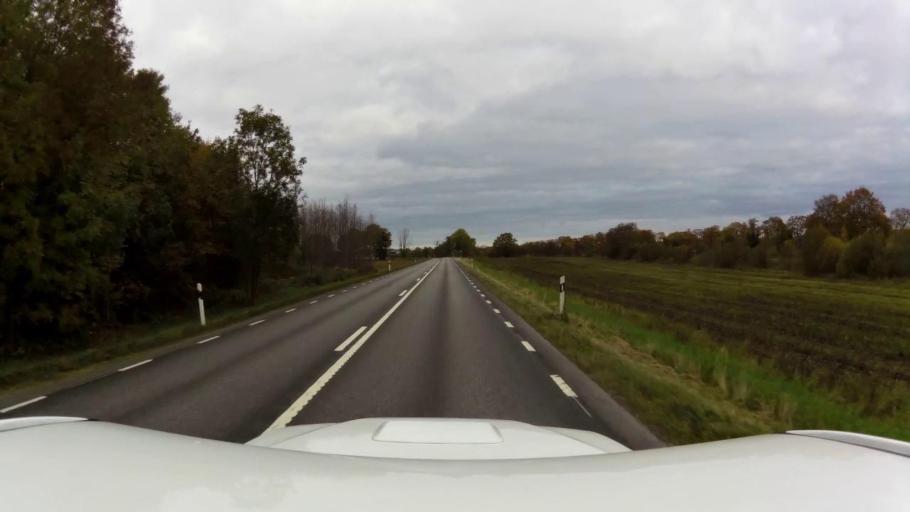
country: SE
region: OEstergoetland
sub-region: Linkopings Kommun
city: Ljungsbro
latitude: 58.5147
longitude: 15.4382
